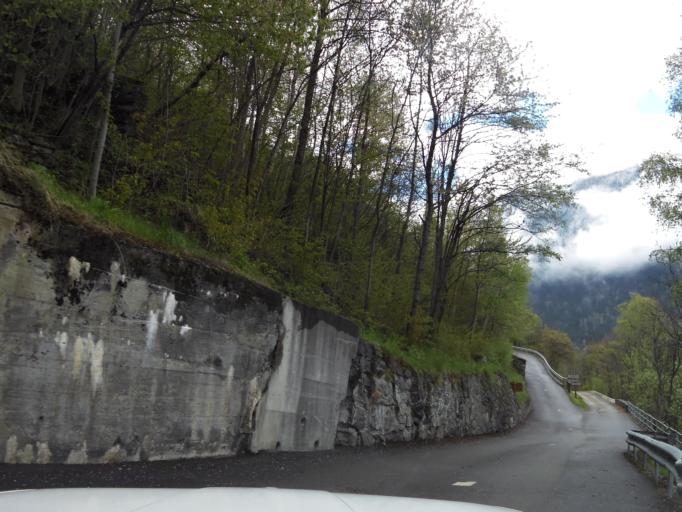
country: FR
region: Rhone-Alpes
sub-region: Departement de la Savoie
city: Saint-Michel-de-Maurienne
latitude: 45.2129
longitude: 6.5511
